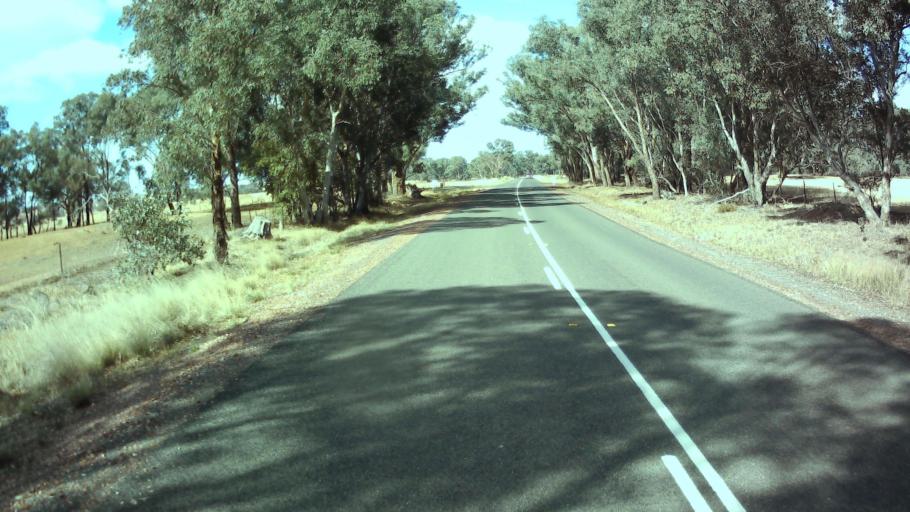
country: AU
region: New South Wales
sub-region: Weddin
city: Grenfell
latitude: -33.9852
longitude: 148.4146
